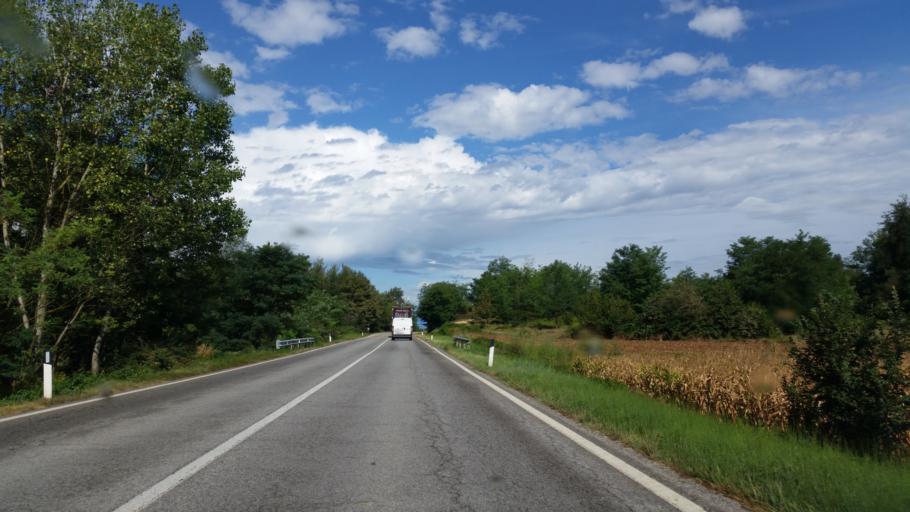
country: IT
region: Piedmont
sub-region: Provincia di Cuneo
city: Monta
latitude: 44.8300
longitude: 7.9288
